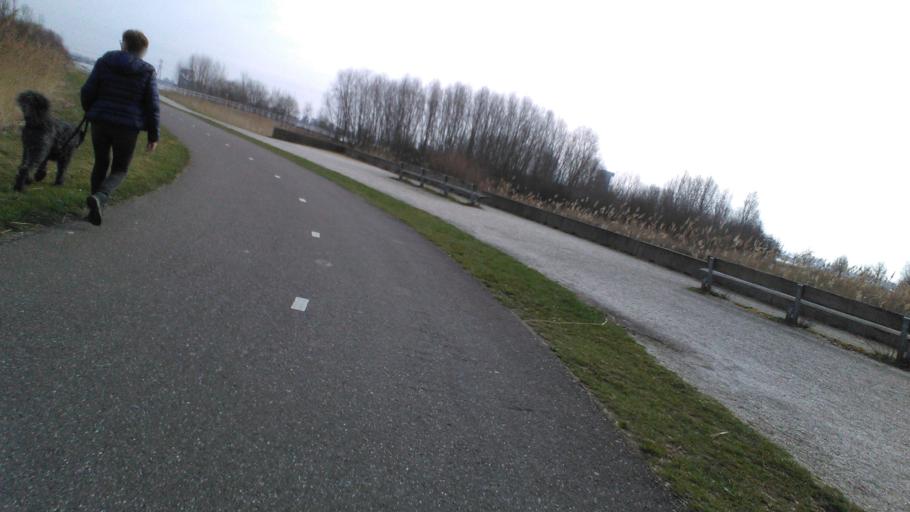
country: NL
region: South Holland
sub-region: Gemeente Lansingerland
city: Bleiswijk
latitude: 51.9839
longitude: 4.5658
